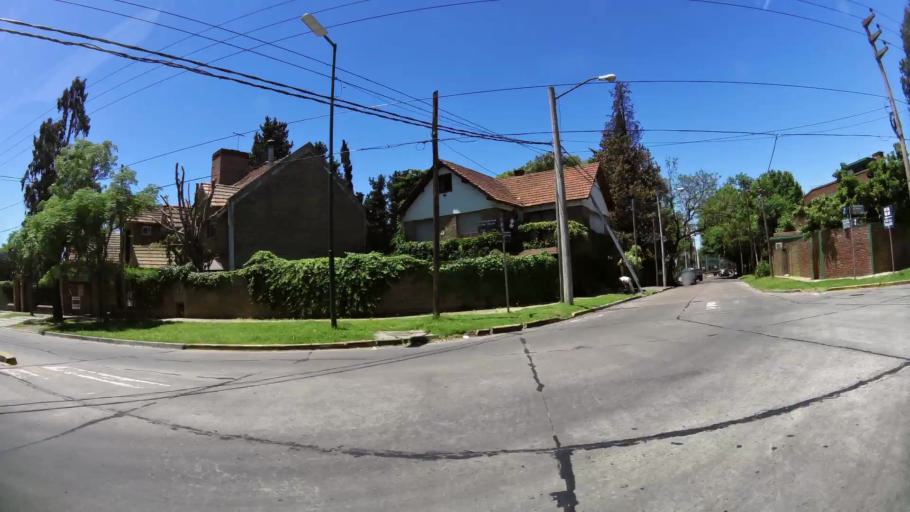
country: AR
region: Buenos Aires
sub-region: Partido de San Isidro
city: San Isidro
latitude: -34.5006
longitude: -58.5604
